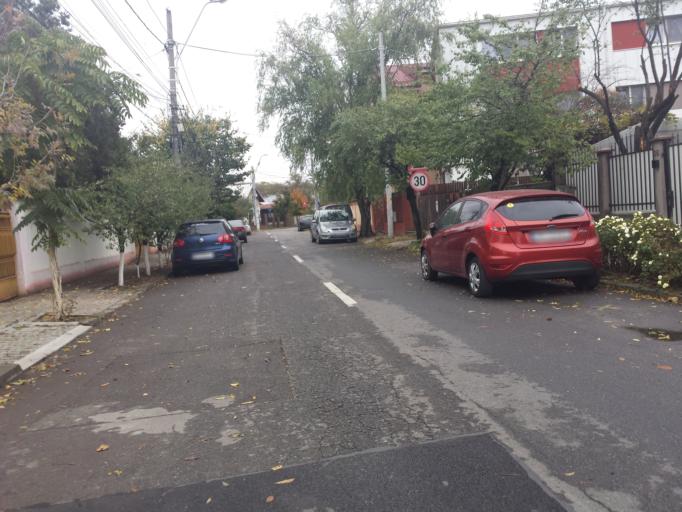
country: RO
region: Ilfov
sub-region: Comuna Chiajna
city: Rosu
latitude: 44.4860
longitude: 26.0309
